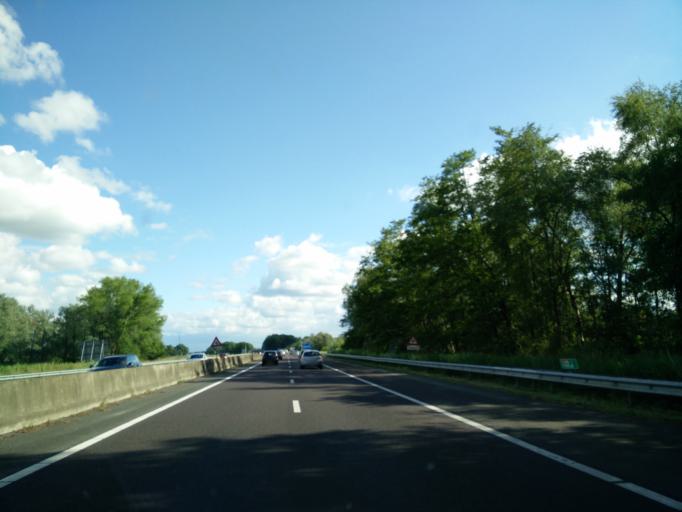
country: NL
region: Groningen
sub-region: Gemeente Haren
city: Haren
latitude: 53.1360
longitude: 6.6083
